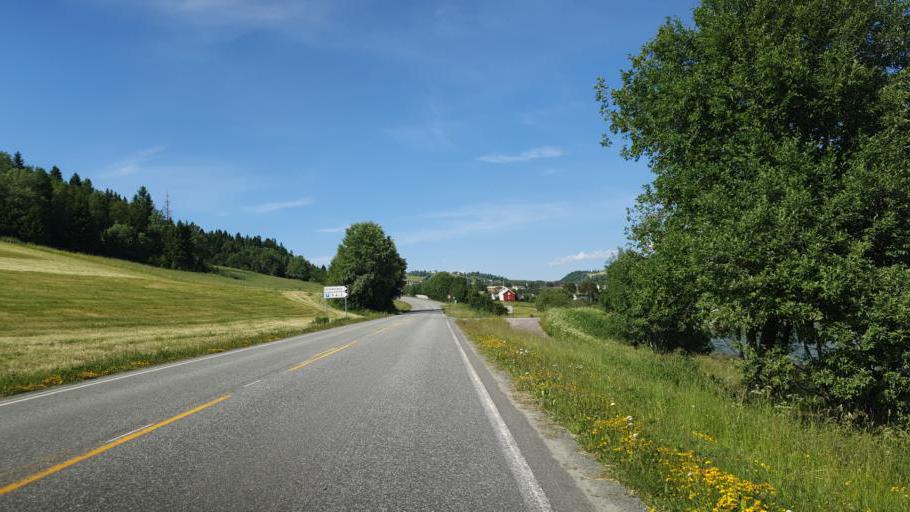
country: NO
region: Nord-Trondelag
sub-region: Leksvik
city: Leksvik
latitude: 63.6616
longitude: 10.6082
